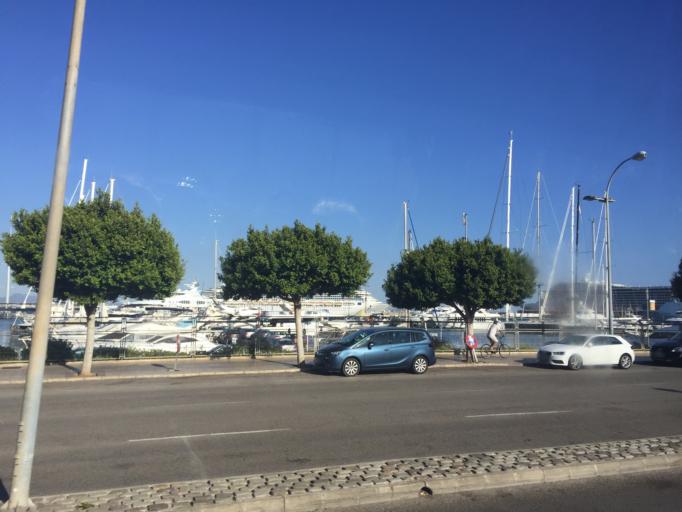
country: ES
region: Balearic Islands
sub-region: Illes Balears
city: Palma
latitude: 39.5587
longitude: 2.6265
